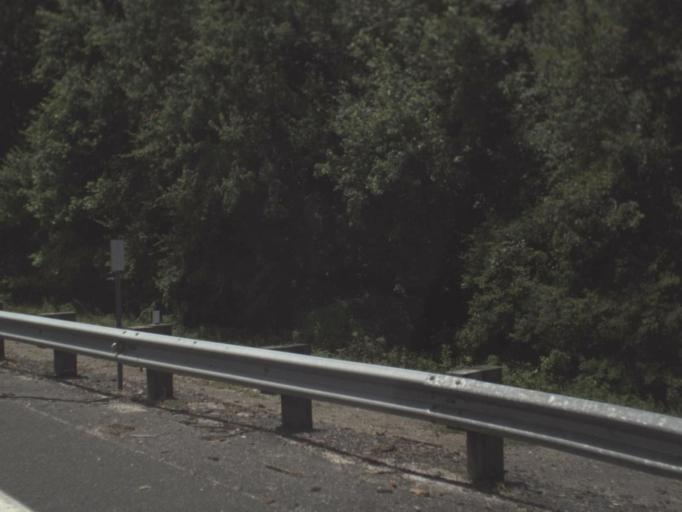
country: US
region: Florida
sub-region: Taylor County
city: Perry
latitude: 30.0663
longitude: -83.5585
